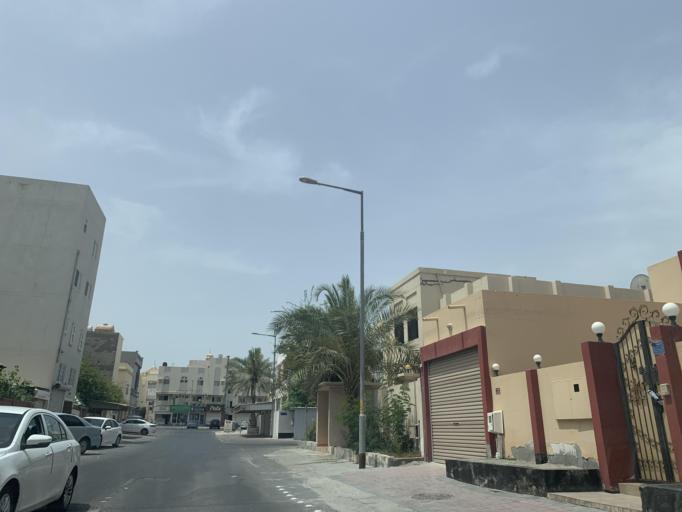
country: BH
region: Northern
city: Ar Rifa'
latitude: 26.1342
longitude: 50.5751
